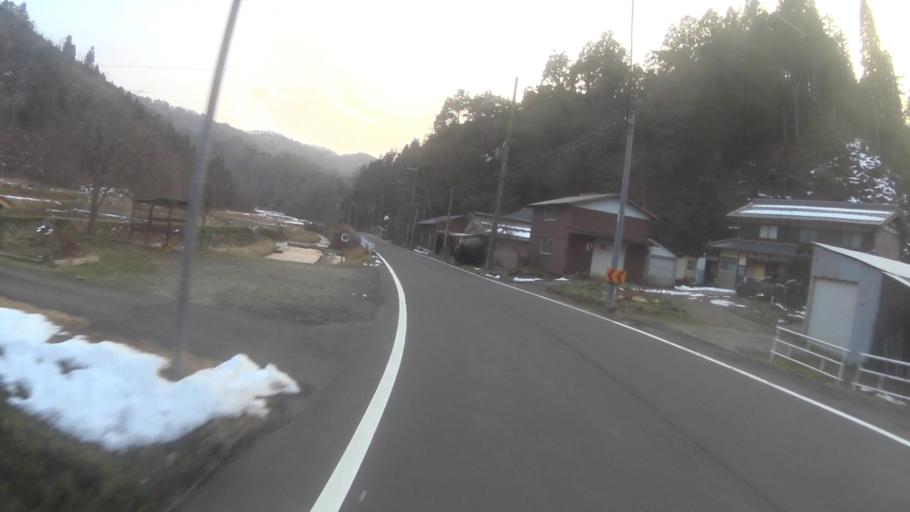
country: JP
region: Kyoto
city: Maizuru
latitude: 35.4306
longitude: 135.4779
